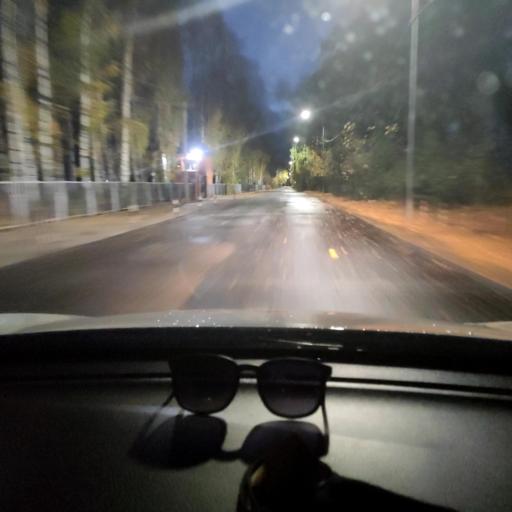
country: RU
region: Tatarstan
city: Verkhniy Uslon
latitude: 55.6030
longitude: 49.0208
